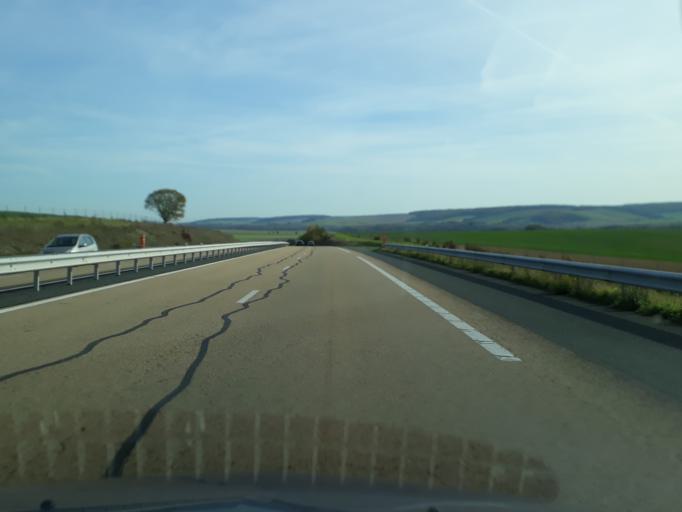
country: FR
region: Champagne-Ardenne
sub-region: Departement de l'Aube
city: Aix-en-Othe
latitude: 48.2673
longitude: 3.7345
